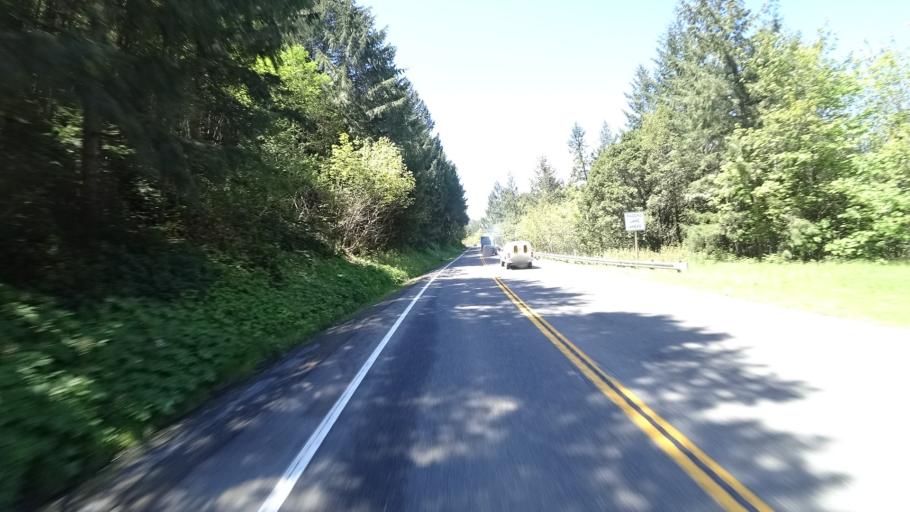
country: US
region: California
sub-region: Humboldt County
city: Blue Lake
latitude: 40.9050
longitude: -123.8192
